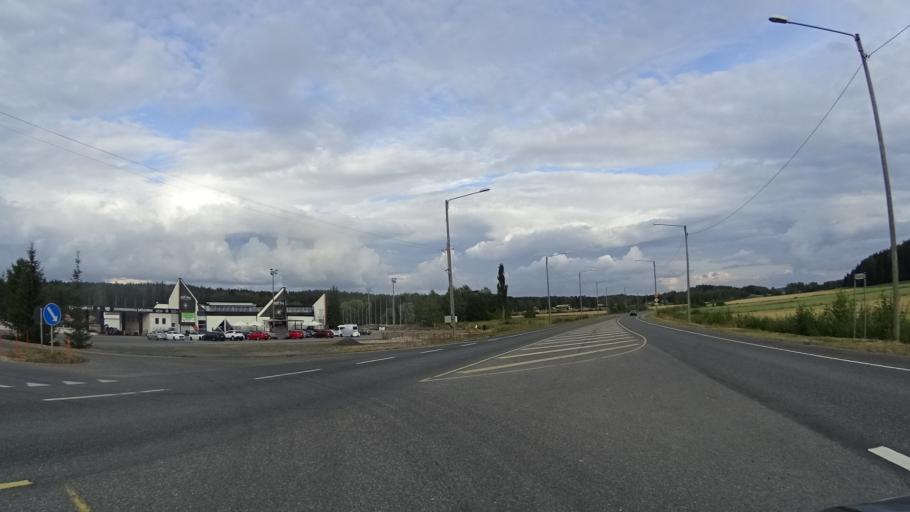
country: FI
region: Haeme
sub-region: Haemeenlinna
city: Parola
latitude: 61.0246
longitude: 24.3254
